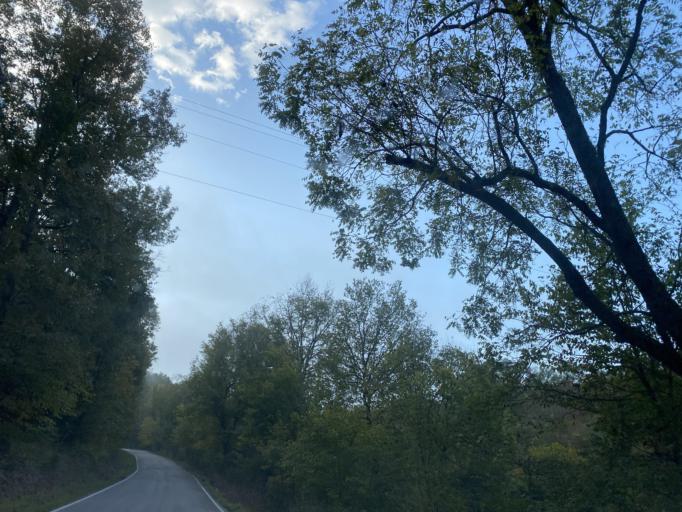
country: US
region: Kentucky
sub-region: Pendleton County
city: Falmouth
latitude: 38.7463
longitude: -84.3175
